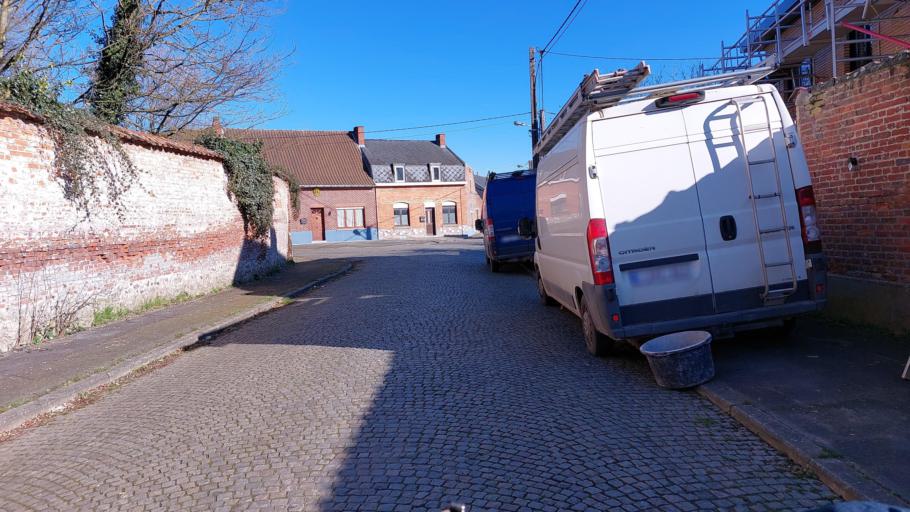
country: BE
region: Wallonia
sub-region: Province du Hainaut
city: Chievres
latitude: 50.5823
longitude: 3.7763
